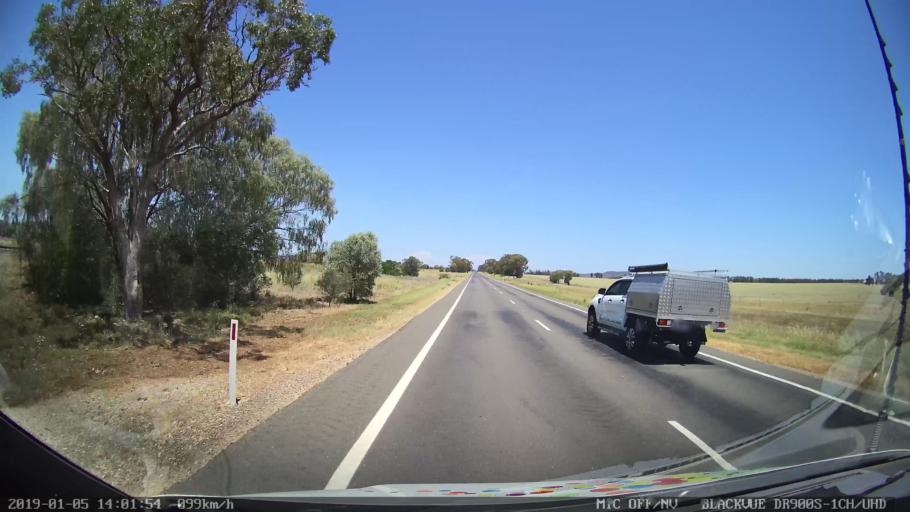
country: AU
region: New South Wales
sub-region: Gunnedah
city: Gunnedah
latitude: -31.1743
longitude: 150.3308
